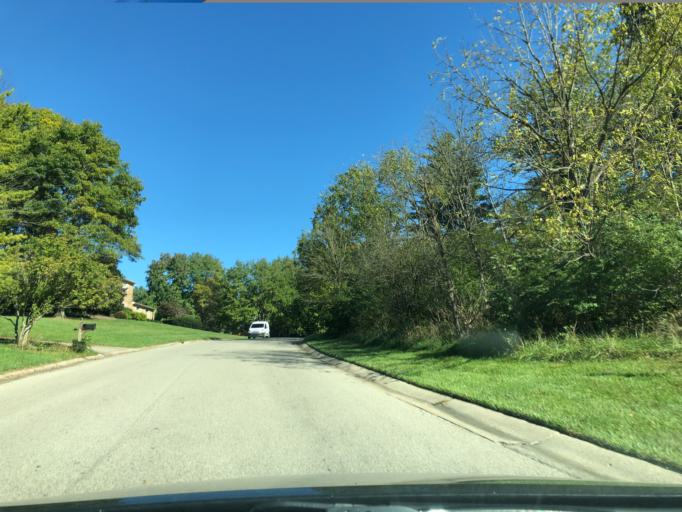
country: US
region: Ohio
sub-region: Hamilton County
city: The Village of Indian Hill
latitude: 39.2571
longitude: -84.2943
